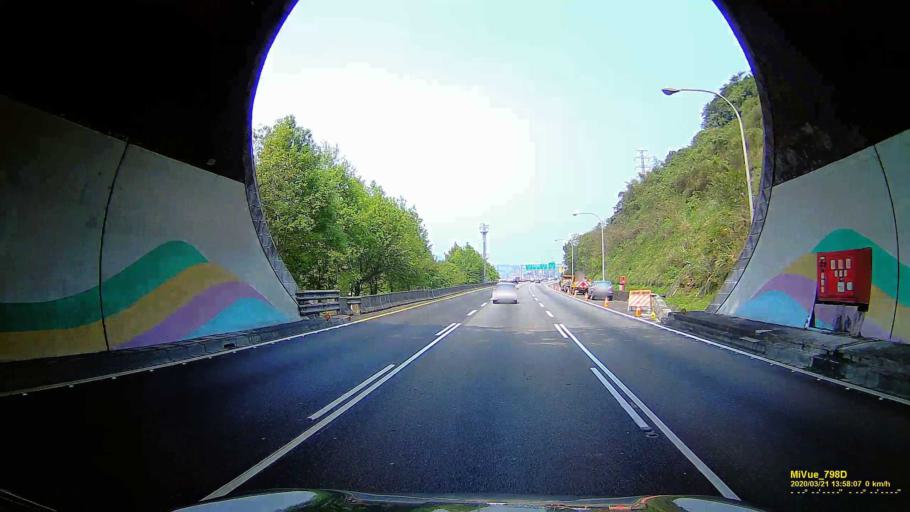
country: TW
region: Taipei
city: Taipei
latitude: 24.9696
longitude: 121.5505
